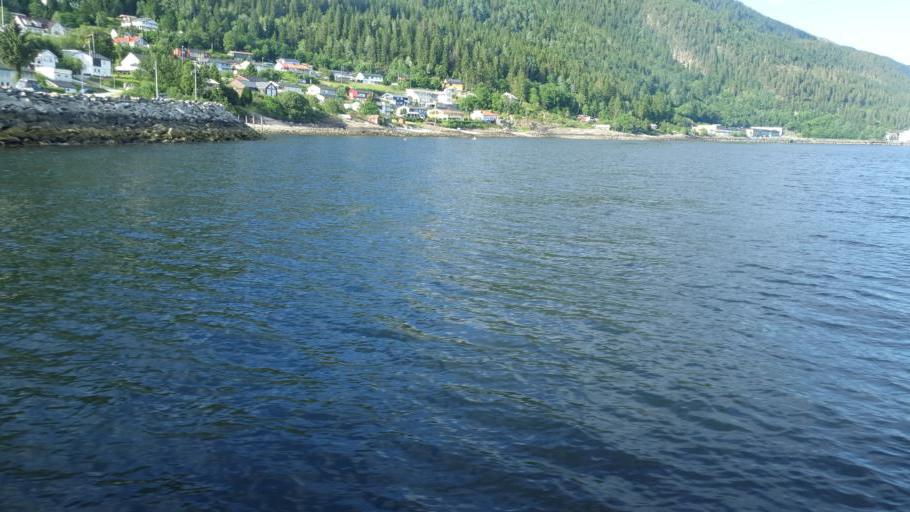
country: NO
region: Sor-Trondelag
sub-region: Trondheim
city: Trondheim
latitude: 63.5533
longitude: 10.2253
